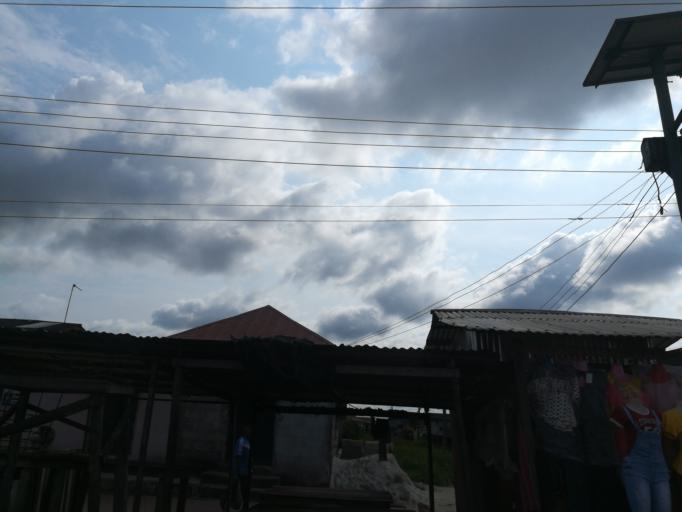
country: NG
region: Rivers
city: Okrika
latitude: 4.7475
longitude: 7.0840
